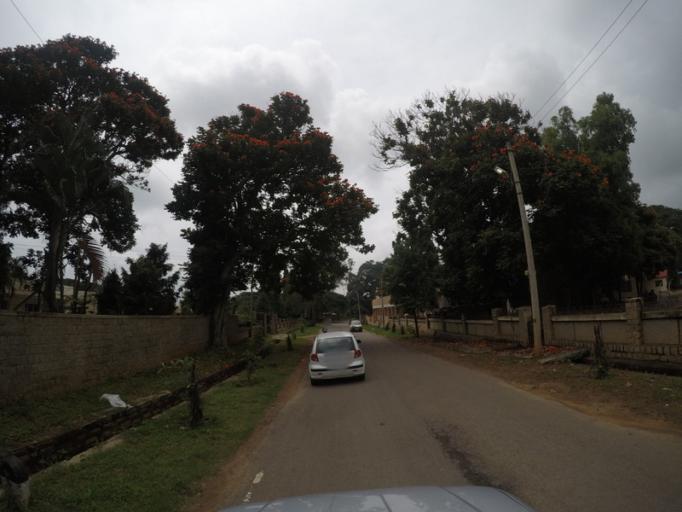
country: IN
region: Karnataka
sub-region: Bangalore Rural
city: Nelamangala
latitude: 13.1361
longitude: 77.4918
